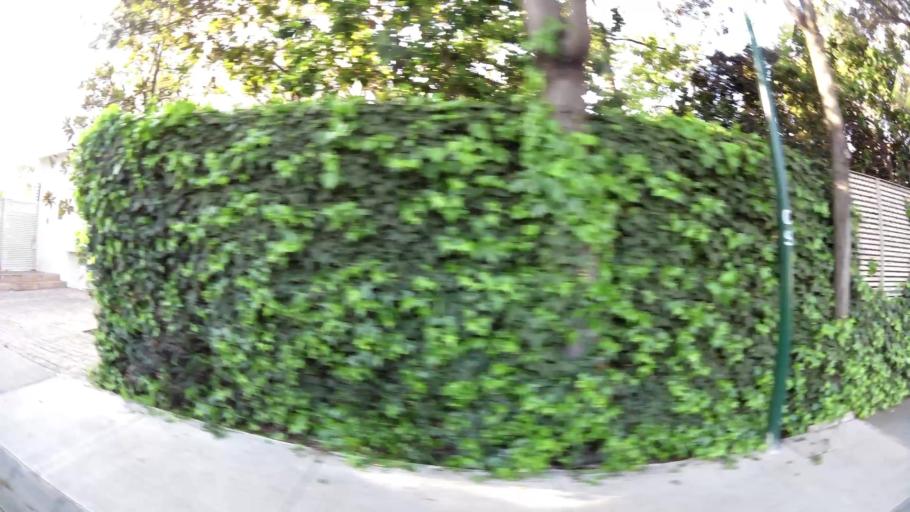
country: CL
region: Santiago Metropolitan
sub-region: Provincia de Santiago
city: Villa Presidente Frei, Nunoa, Santiago, Chile
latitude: -33.3504
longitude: -70.5379
